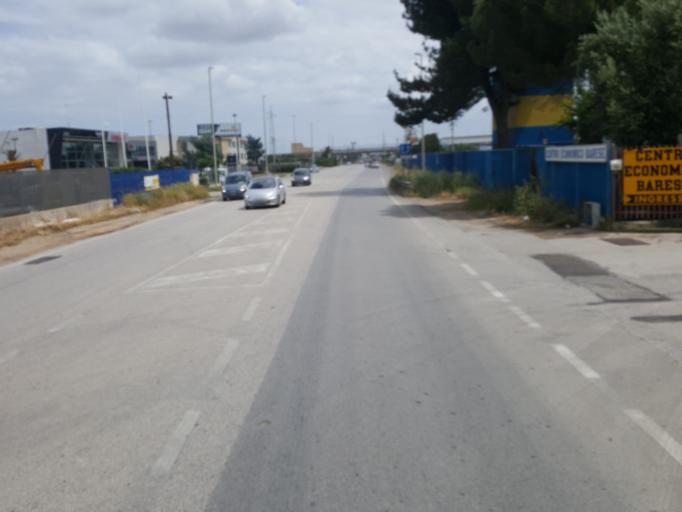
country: IT
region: Apulia
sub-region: Provincia di Bari
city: Modugno
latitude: 41.0930
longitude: 16.7529
